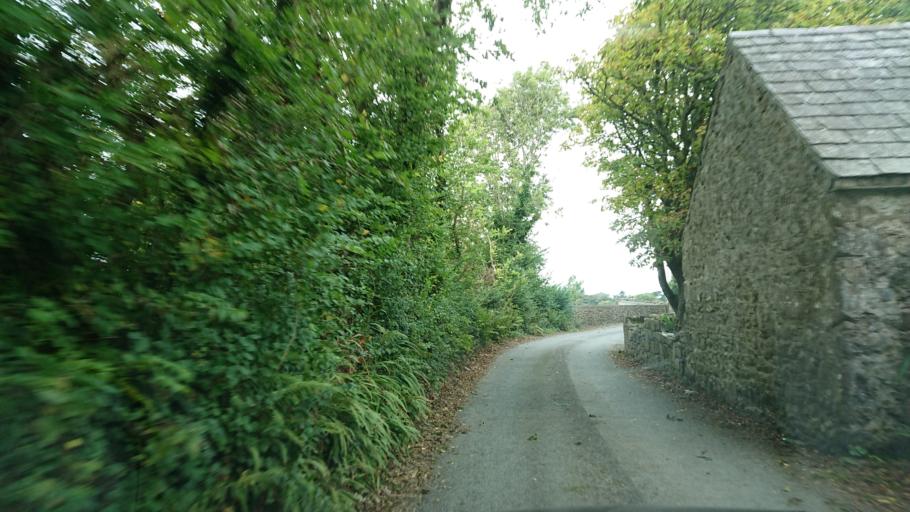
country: IE
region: Munster
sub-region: Waterford
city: Waterford
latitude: 52.2133
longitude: -7.0426
